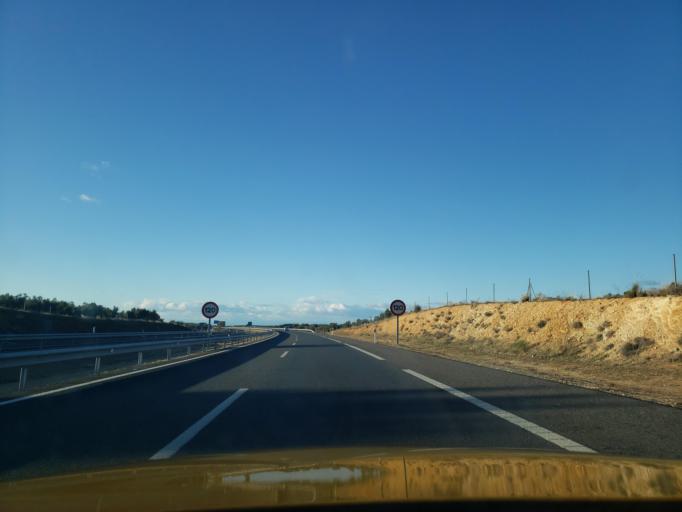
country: ES
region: Castille-La Mancha
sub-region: Province of Toledo
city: Nambroca
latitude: 39.7990
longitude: -3.9595
